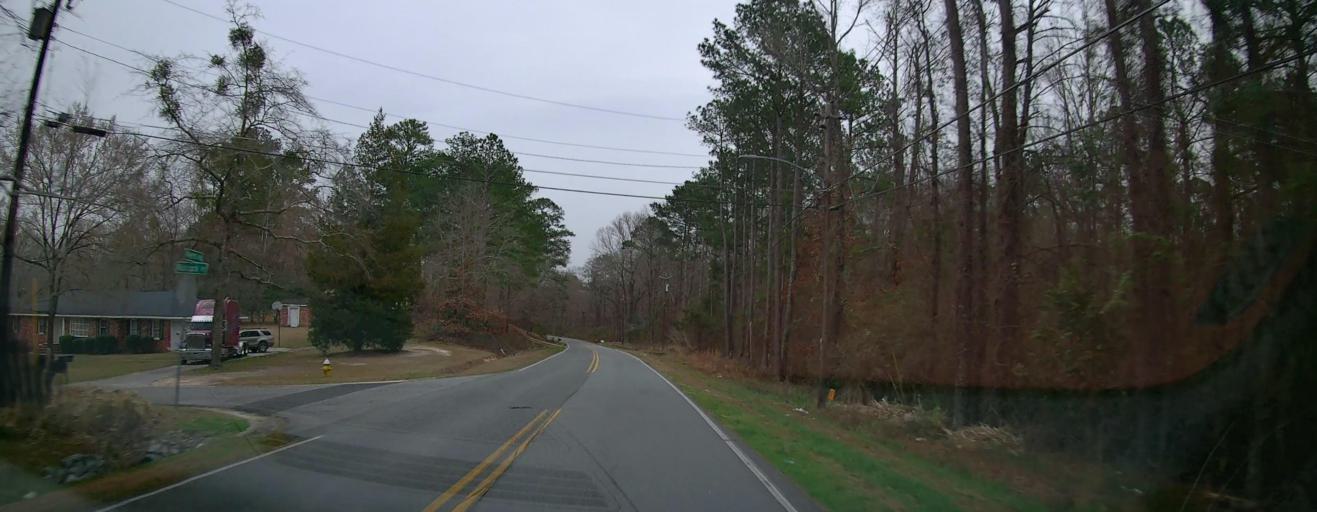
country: US
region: Georgia
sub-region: Bibb County
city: Macon
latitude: 32.8590
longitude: -83.7206
